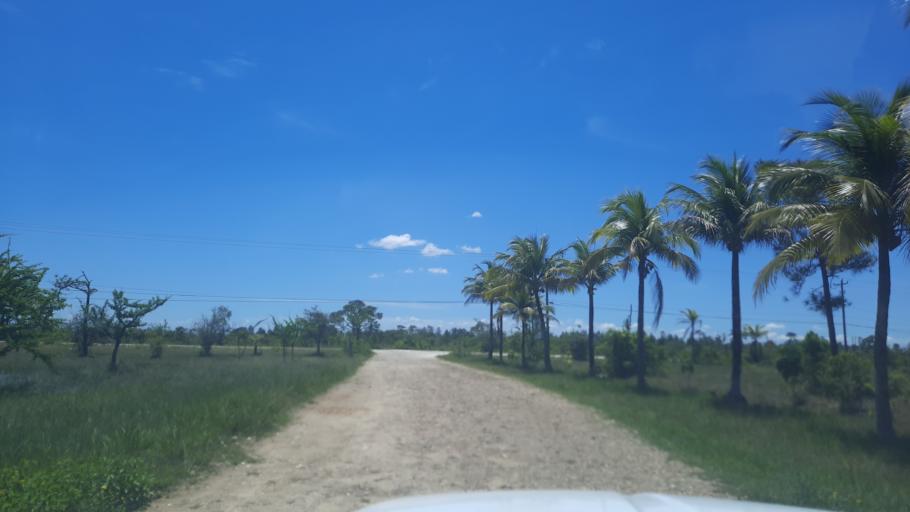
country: BZ
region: Cayo
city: Belmopan
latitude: 17.3242
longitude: -88.5649
